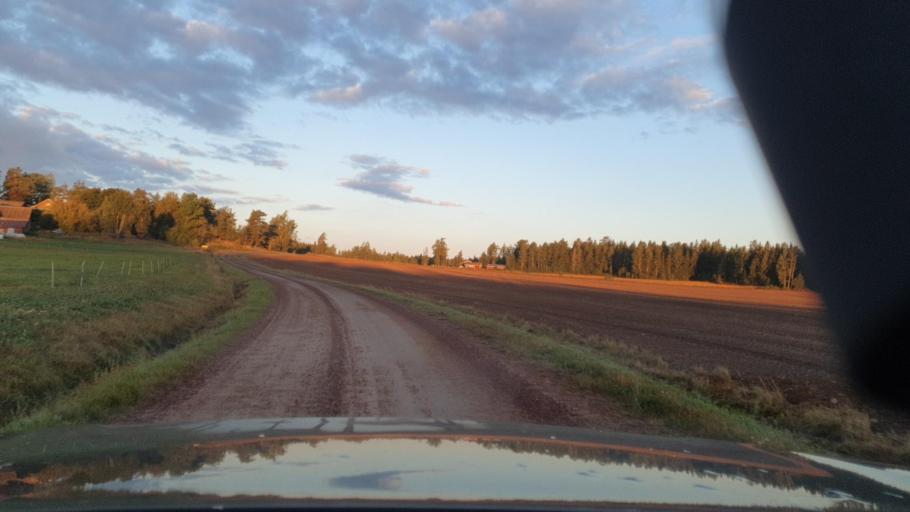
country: SE
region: Vaermland
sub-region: Kristinehamns Kommun
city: Kristinehamn
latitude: 59.4185
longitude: 13.9882
